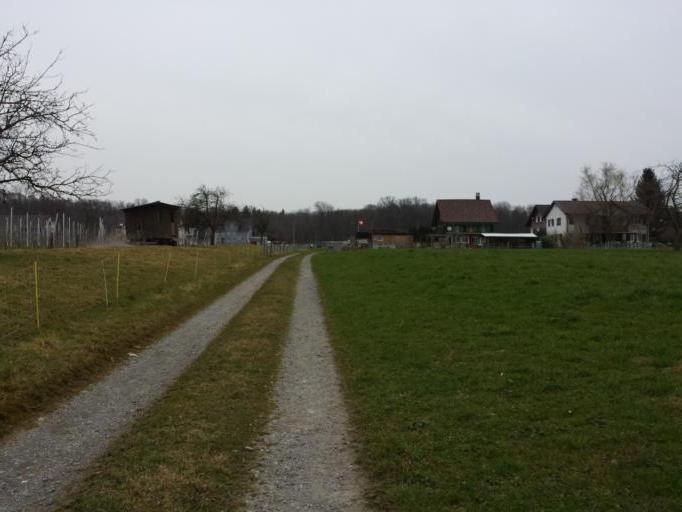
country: CH
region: Thurgau
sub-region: Arbon District
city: Salmsach
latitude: 47.5584
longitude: 9.3487
